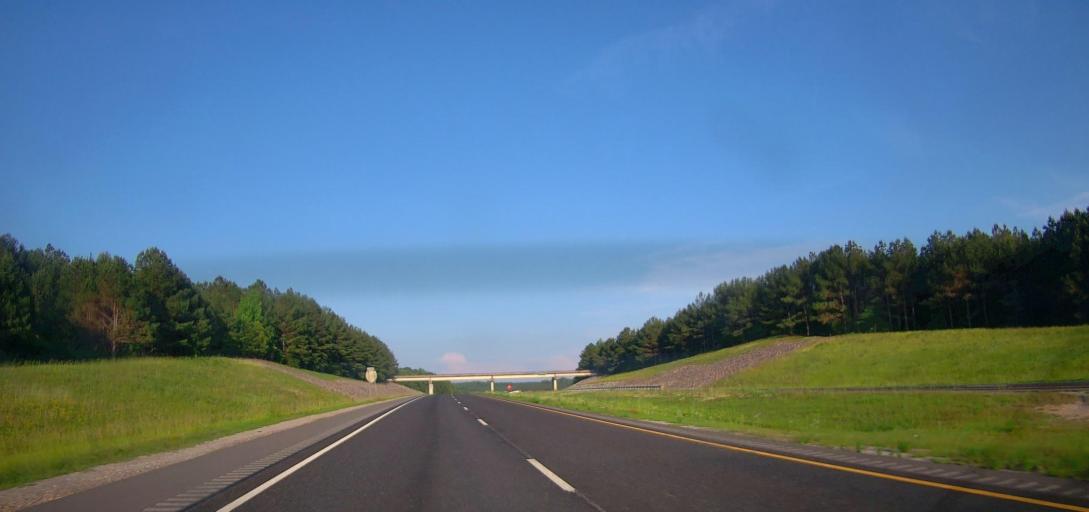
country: US
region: Alabama
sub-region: Marion County
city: Guin
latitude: 34.0452
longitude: -87.8997
